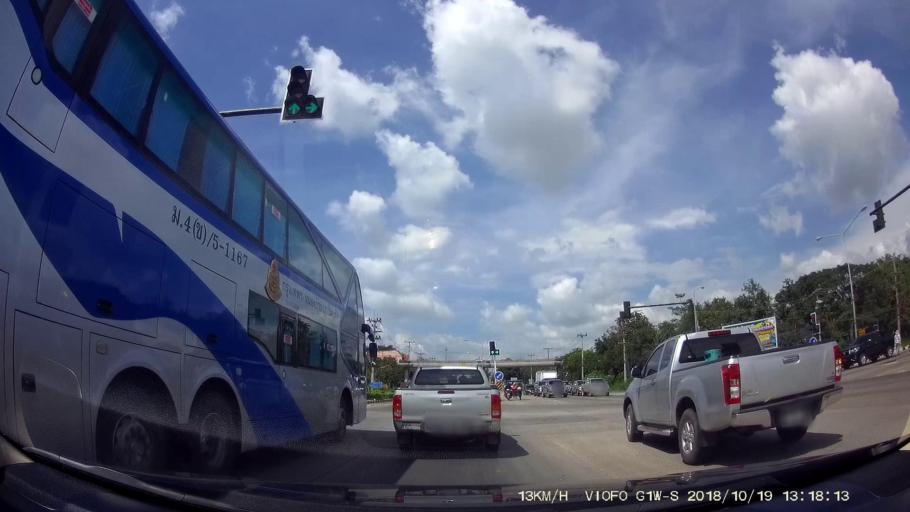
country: TH
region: Chaiyaphum
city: Chatturat
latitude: 15.4142
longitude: 101.8335
